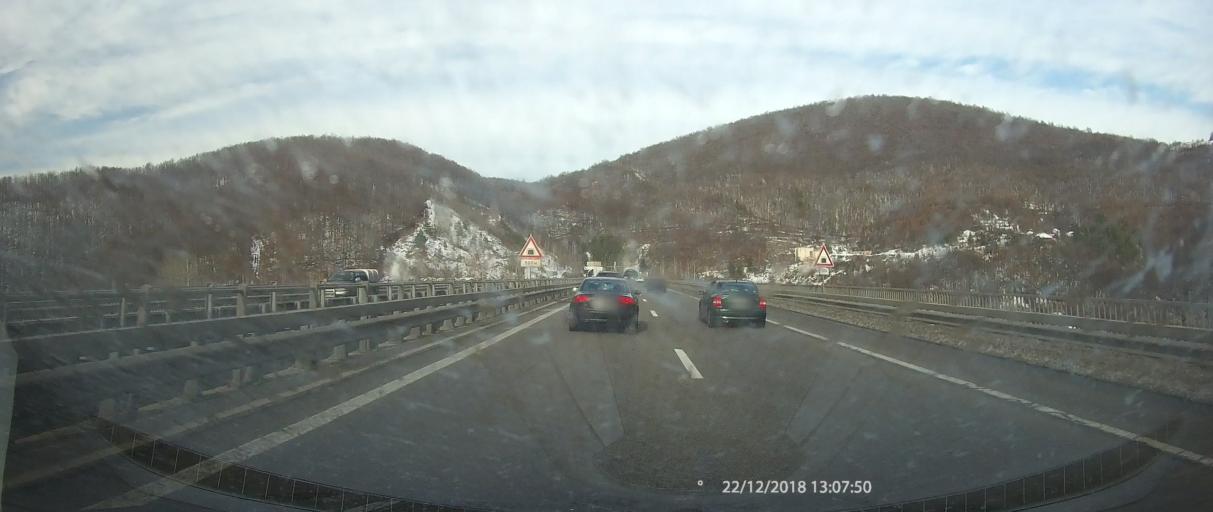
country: BG
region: Sofiya
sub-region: Obshtina Botevgrad
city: Botevgrad
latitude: 42.8283
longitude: 23.7967
